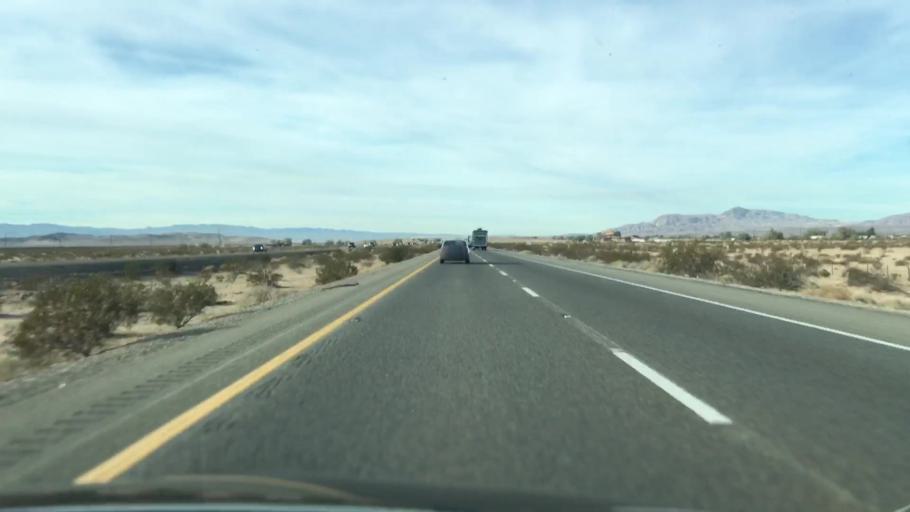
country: US
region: California
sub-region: San Bernardino County
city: Fort Irwin
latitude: 34.9686
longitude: -116.6339
